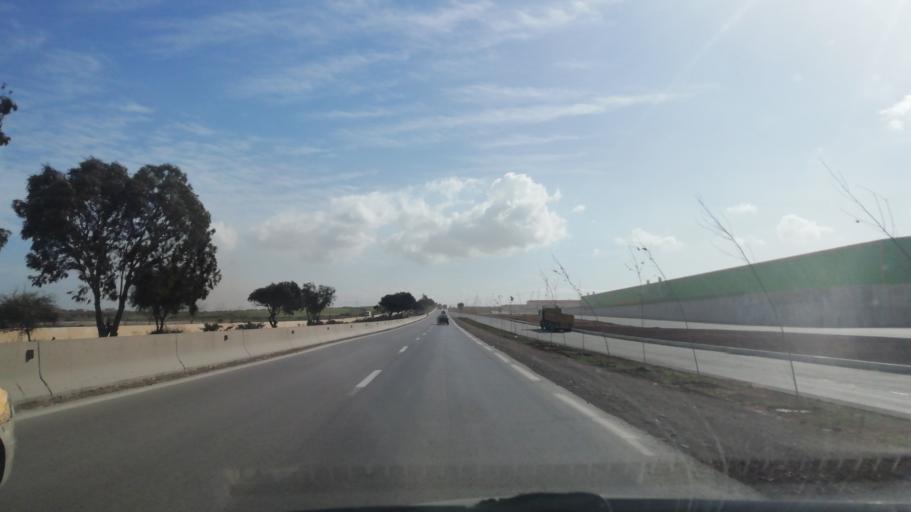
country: DZ
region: Oran
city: Ain el Bya
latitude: 35.7756
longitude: -0.2560
